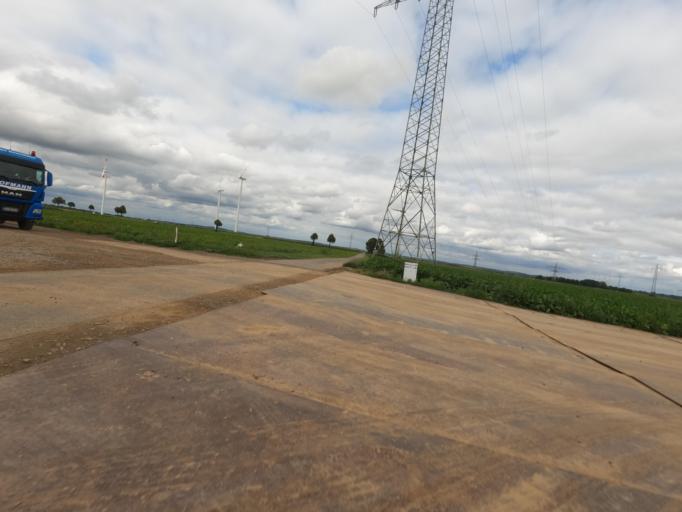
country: DE
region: North Rhine-Westphalia
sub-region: Regierungsbezirk Koln
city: Linnich
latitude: 50.9841
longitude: 6.2366
